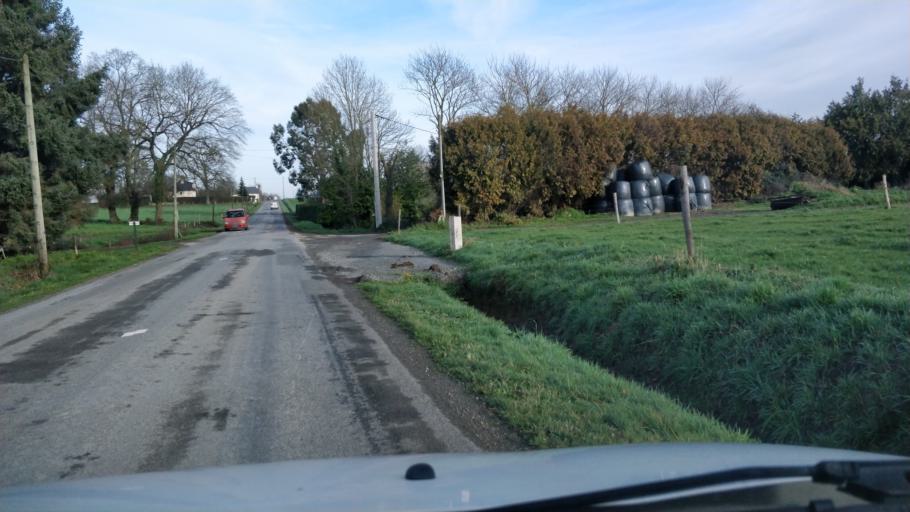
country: FR
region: Brittany
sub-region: Departement d'Ille-et-Vilaine
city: Argentre-du-Plessis
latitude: 48.0321
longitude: -1.1674
